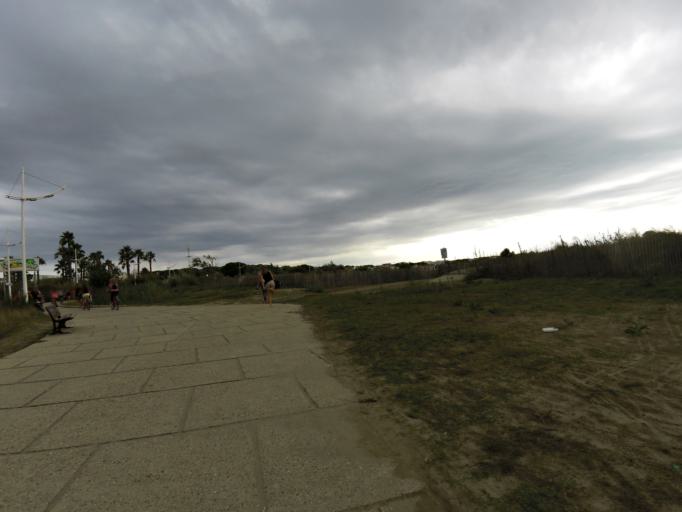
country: FR
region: Languedoc-Roussillon
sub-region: Departement du Gard
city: Le Grau-du-Roi
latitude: 43.5286
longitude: 4.1399
